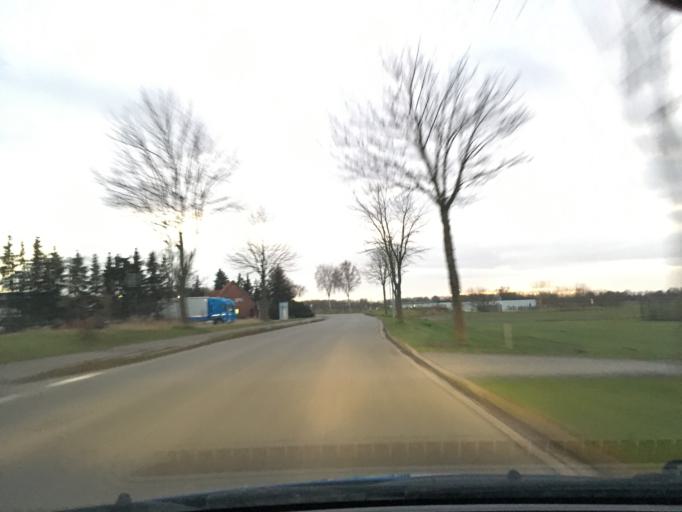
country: DE
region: Lower Saxony
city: Barum
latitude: 53.3647
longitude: 10.4147
